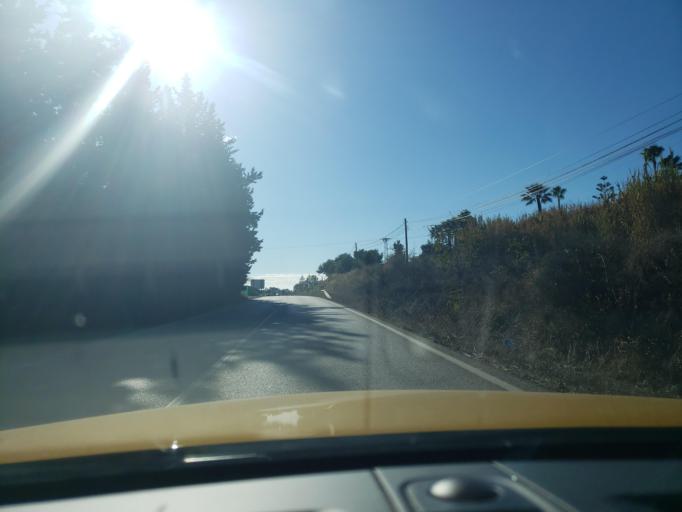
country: ES
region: Andalusia
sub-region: Provincia de Malaga
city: Benahavis
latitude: 36.4784
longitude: -5.0138
